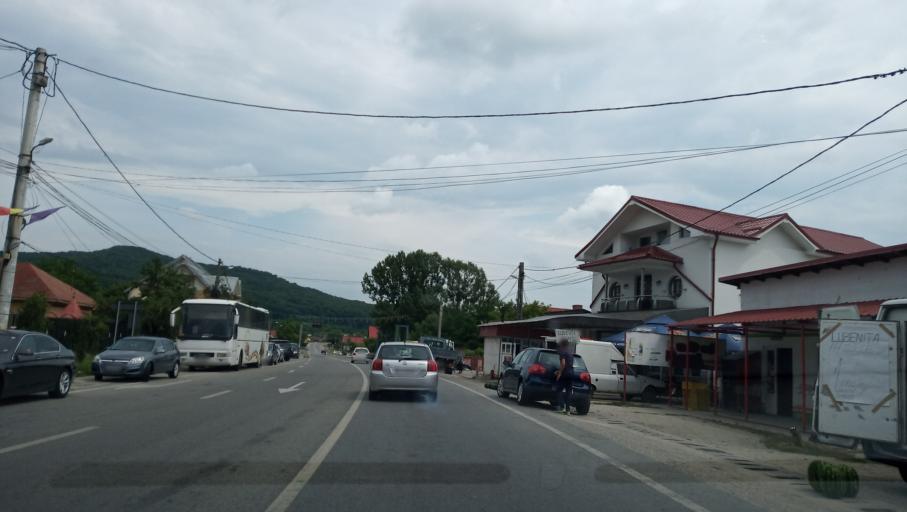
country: RO
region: Gorj
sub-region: Comuna Balteni
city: Pesteana Jiu
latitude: 44.8481
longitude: 23.2973
